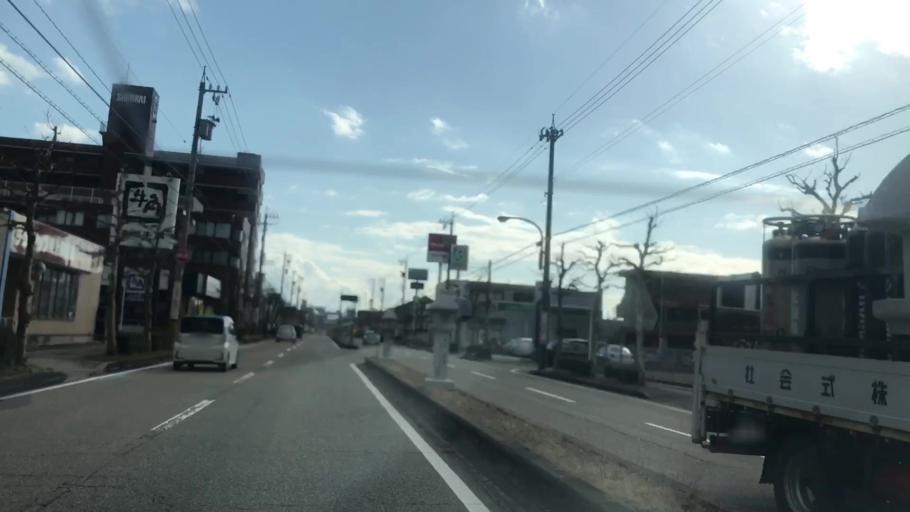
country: JP
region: Toyama
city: Takaoka
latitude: 36.7343
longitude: 137.0155
